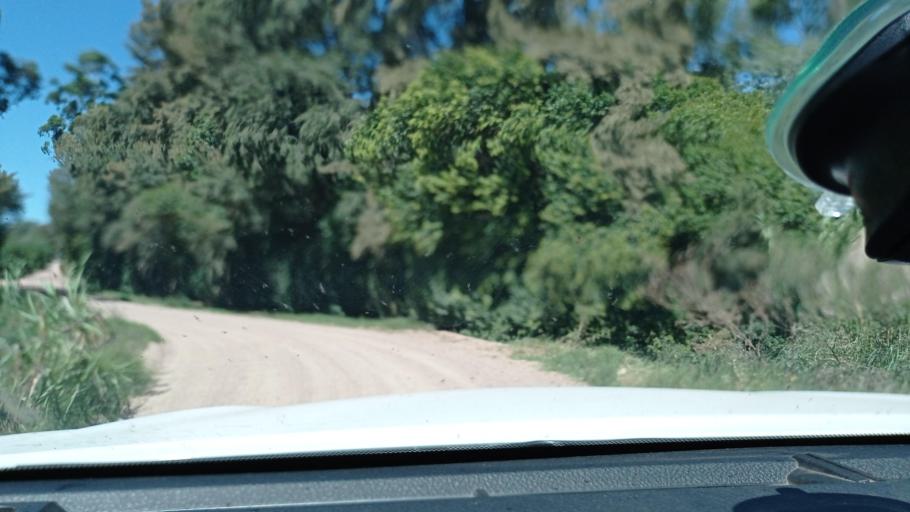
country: UY
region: Canelones
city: La Paz
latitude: -34.7603
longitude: -56.1784
